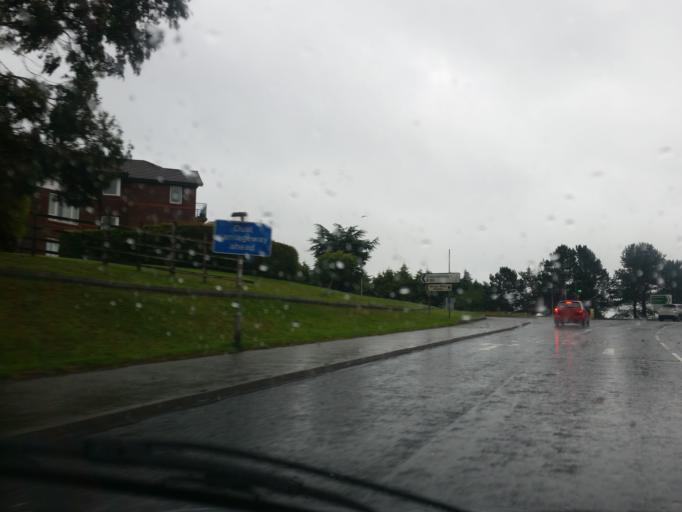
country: GB
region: Northern Ireland
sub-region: North Down District
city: Bangor
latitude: 54.6539
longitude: -5.6955
